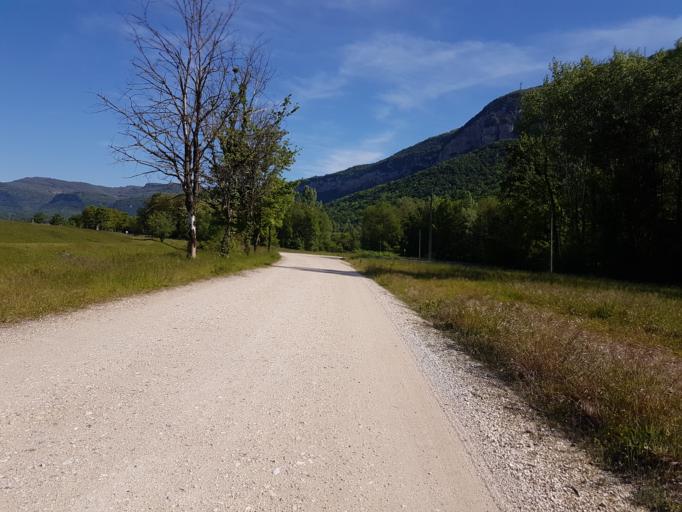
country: FR
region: Rhone-Alpes
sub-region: Departement de l'Ain
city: Villebois
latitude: 45.8257
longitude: 5.4381
